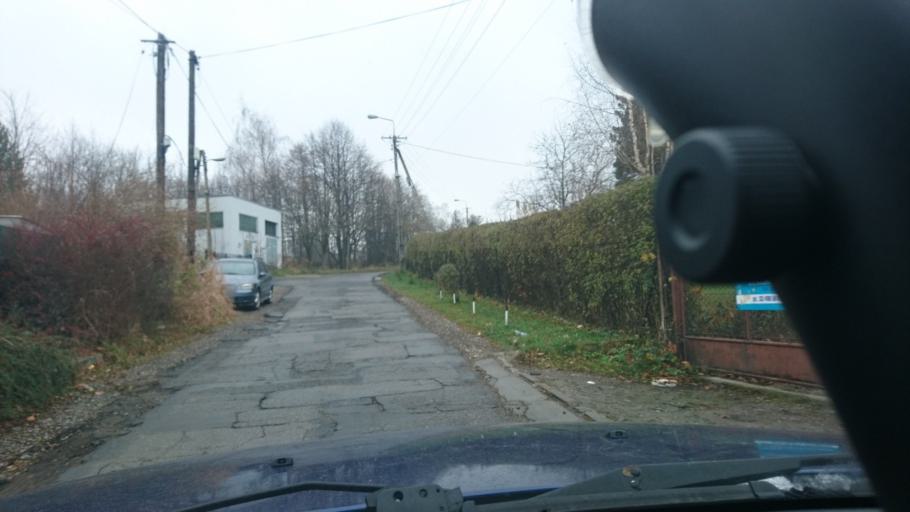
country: PL
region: Silesian Voivodeship
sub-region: Bielsko-Biala
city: Bielsko-Biala
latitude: 49.7957
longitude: 19.0675
